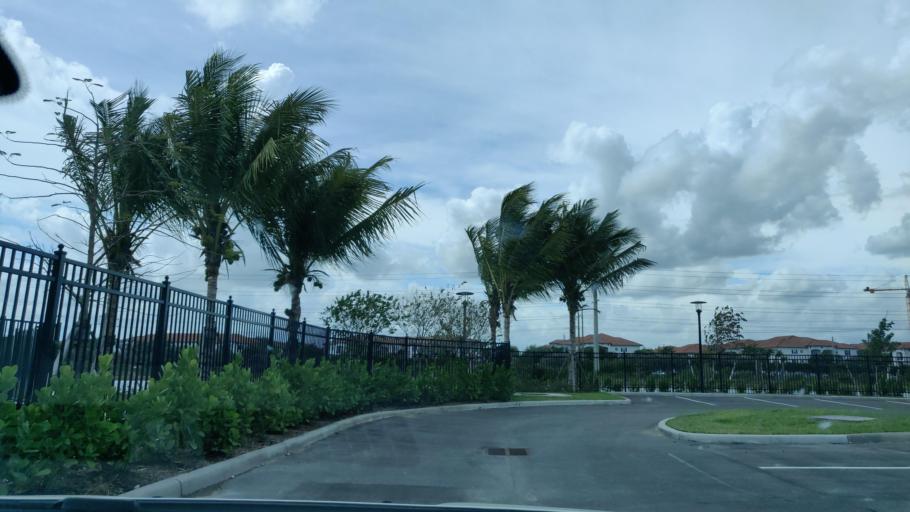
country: US
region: Florida
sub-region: Miami-Dade County
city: Country Club
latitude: 25.9815
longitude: -80.2983
